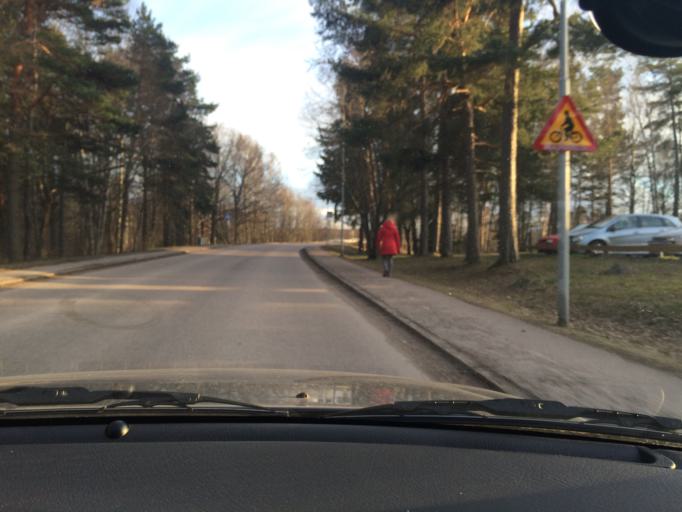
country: SE
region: Vaestmanland
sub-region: Vasteras
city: Vasteras
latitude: 59.6119
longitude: 16.5890
